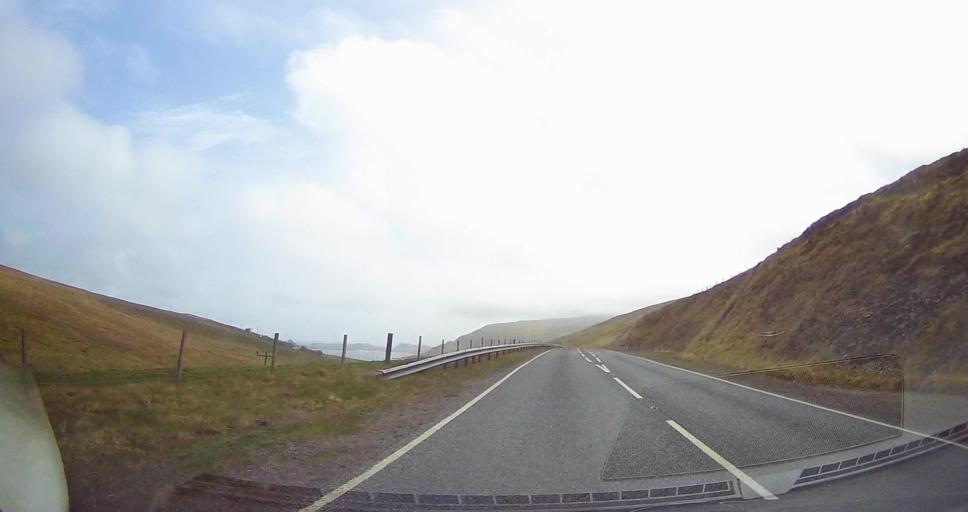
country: GB
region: Scotland
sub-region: Shetland Islands
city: Sandwick
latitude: 60.0014
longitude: -1.2791
